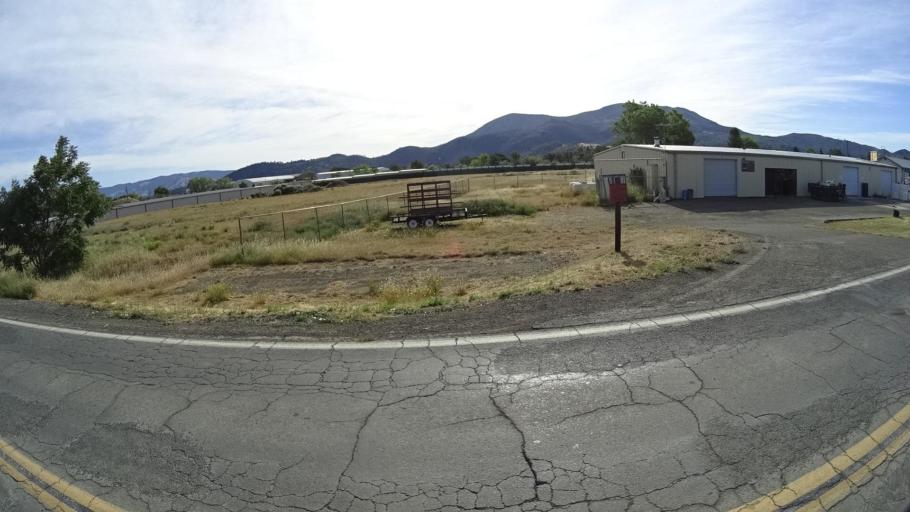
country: US
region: California
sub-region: Lake County
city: Kelseyville
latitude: 38.9834
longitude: -122.8463
